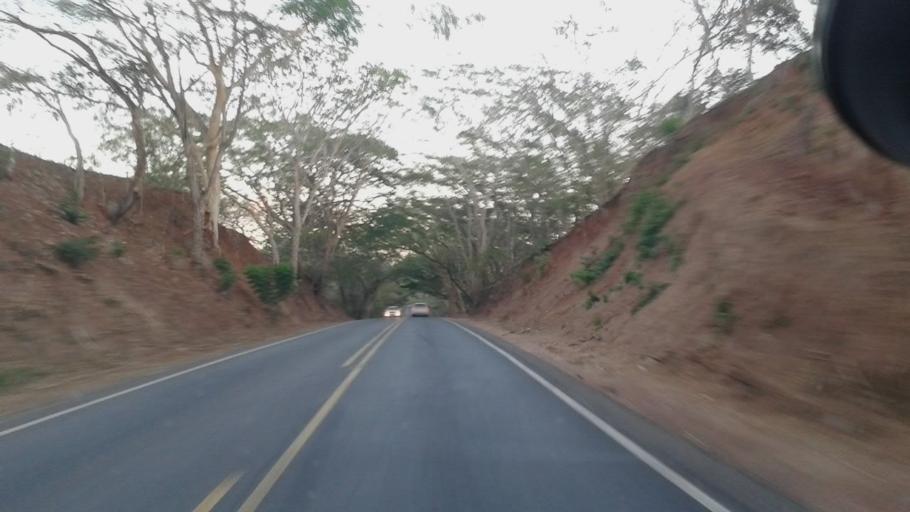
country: CR
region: Puntarenas
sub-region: Canton Central de Puntarenas
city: Puntarenas
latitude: 10.1077
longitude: -84.8835
